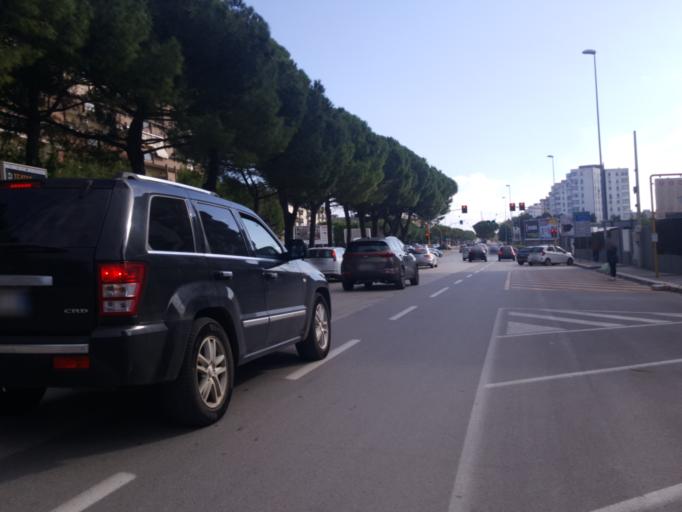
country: IT
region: Apulia
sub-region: Provincia di Bari
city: Bari
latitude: 41.1068
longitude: 16.8980
